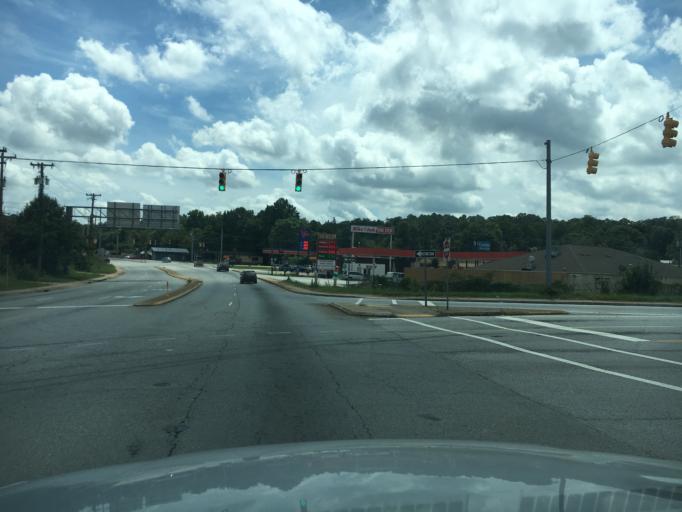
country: US
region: South Carolina
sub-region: Greenville County
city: Gantt
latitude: 34.7947
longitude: -82.3804
